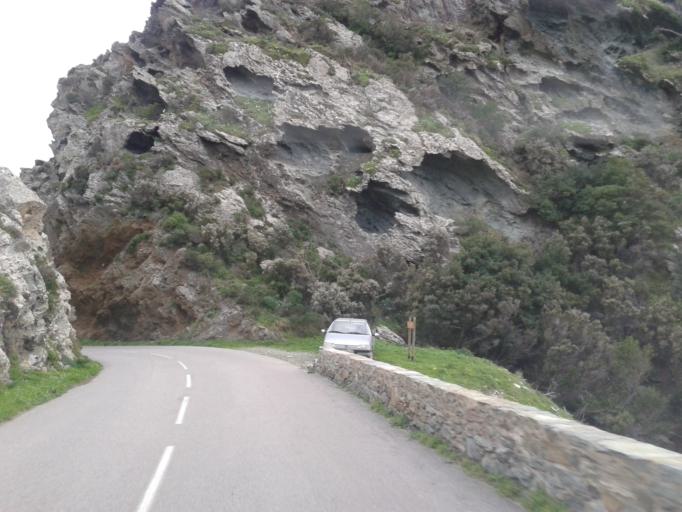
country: FR
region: Corsica
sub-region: Departement de la Haute-Corse
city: Brando
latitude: 42.8771
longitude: 9.3308
